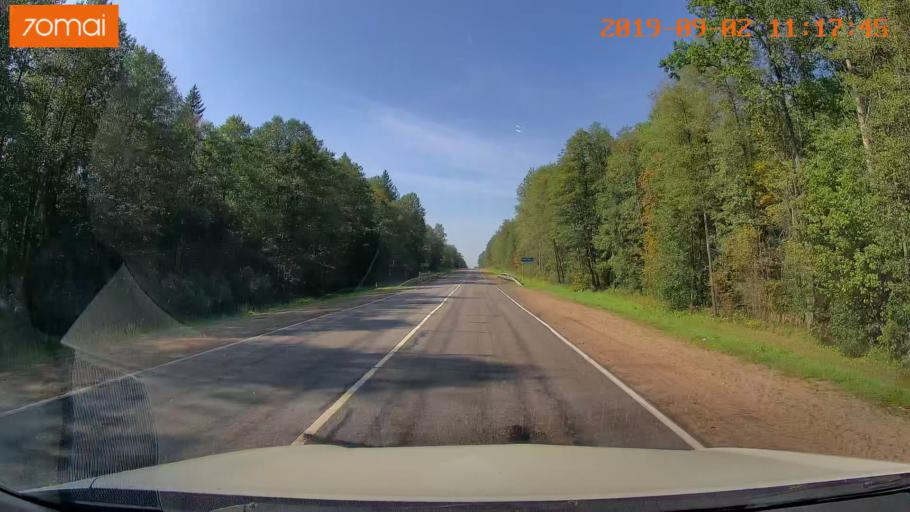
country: RU
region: Smolensk
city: Yekimovichi
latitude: 54.0594
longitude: 33.1108
